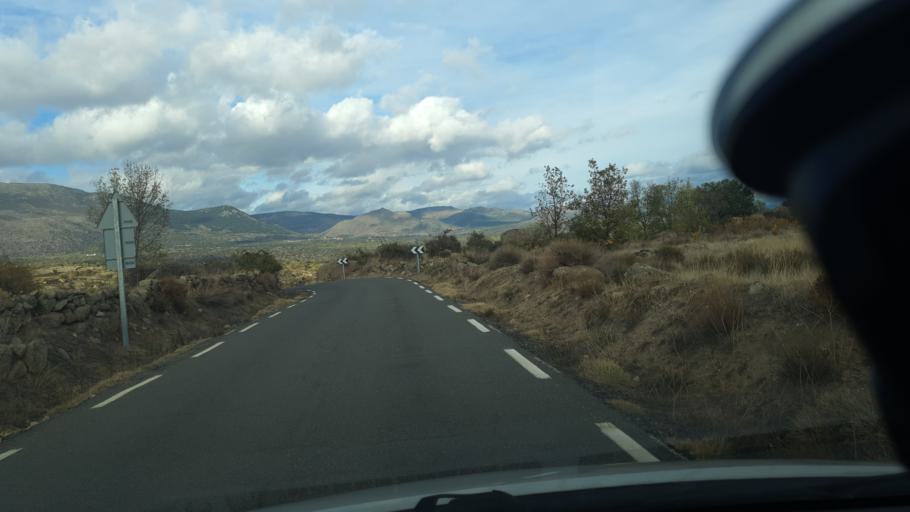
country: ES
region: Castille and Leon
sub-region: Provincia de Avila
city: Burgohondo
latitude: 40.4100
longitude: -4.8129
